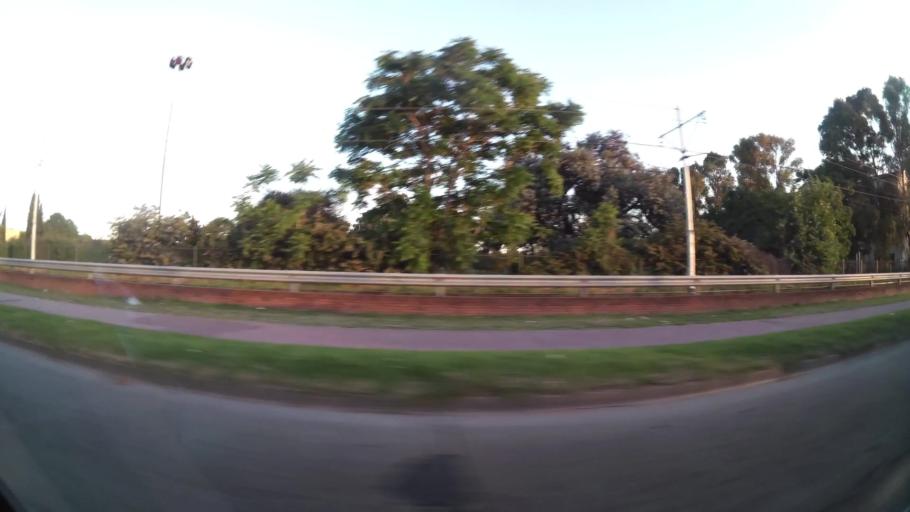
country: AR
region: Buenos Aires F.D.
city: Villa Lugano
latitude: -34.6766
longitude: -58.4629
